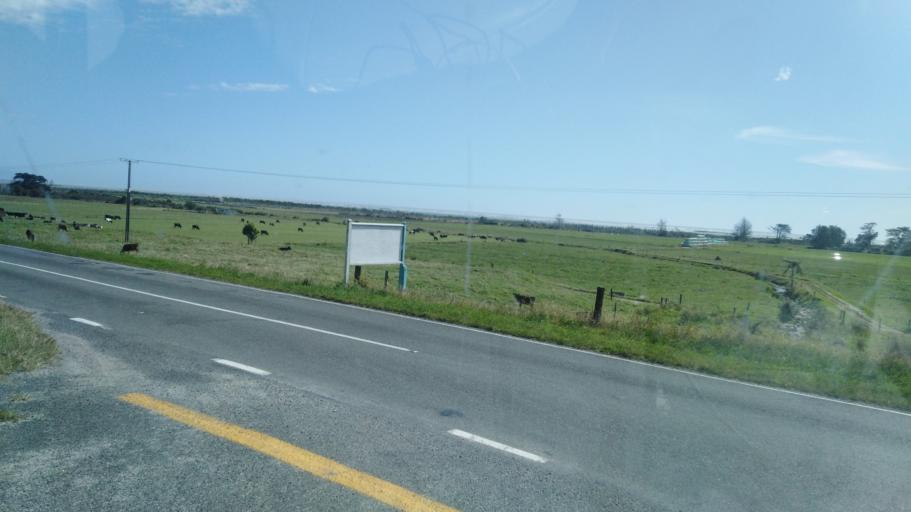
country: NZ
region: West Coast
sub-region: Buller District
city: Westport
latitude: -41.2602
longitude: 172.1127
